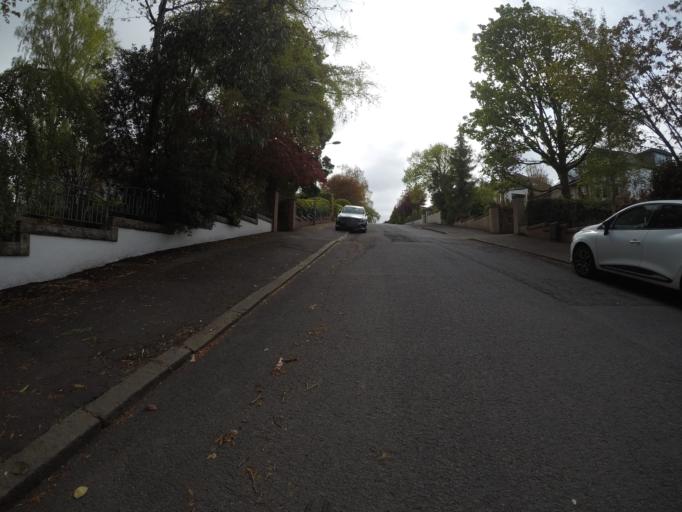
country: GB
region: Scotland
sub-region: East Renfrewshire
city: Giffnock
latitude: 55.7851
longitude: -4.3031
